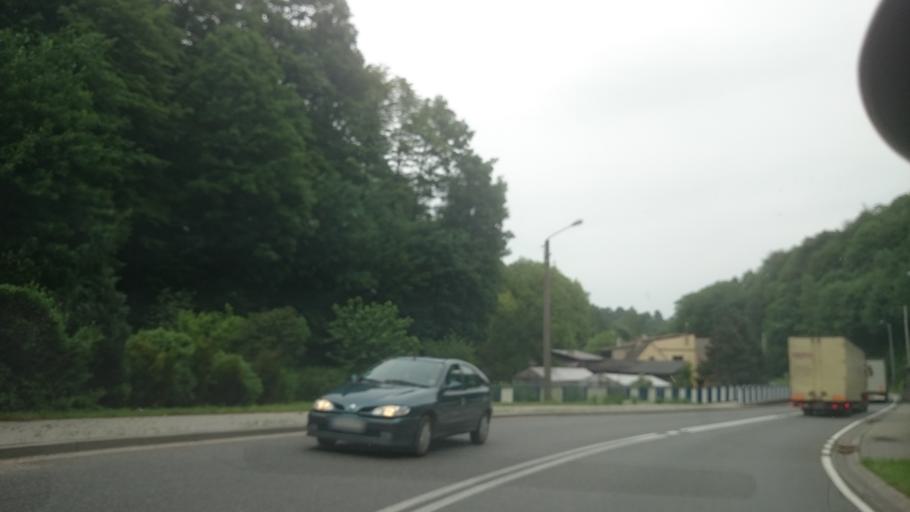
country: PL
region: Lower Silesian Voivodeship
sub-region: Powiat zabkowicki
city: Zloty Stok
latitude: 50.4503
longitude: 16.8387
